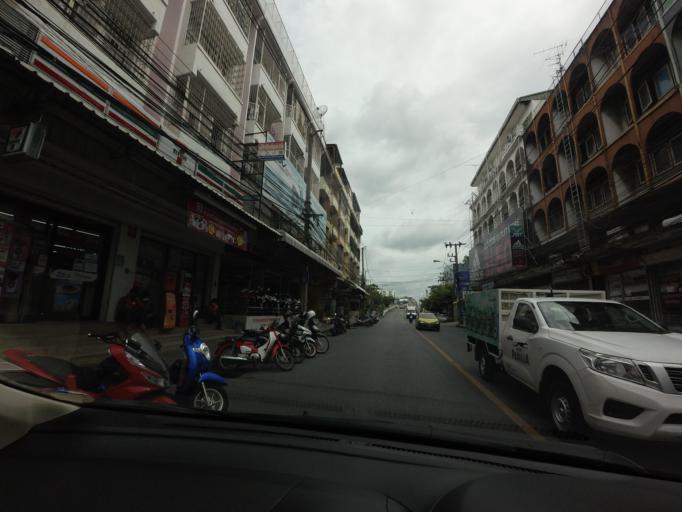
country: TH
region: Bangkok
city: Bang Kapi
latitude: 13.7611
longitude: 100.6243
